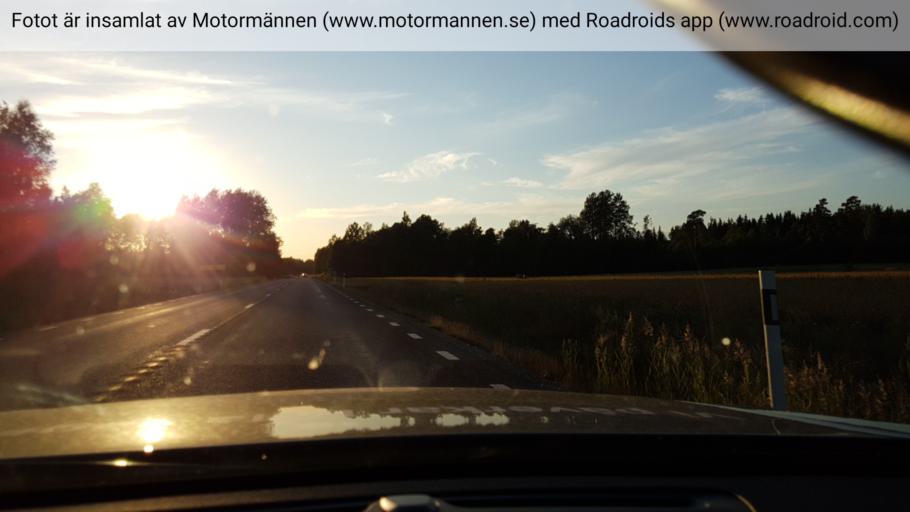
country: SE
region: Vaermland
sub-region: Storfors Kommun
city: Storfors
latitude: 59.4631
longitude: 14.3489
